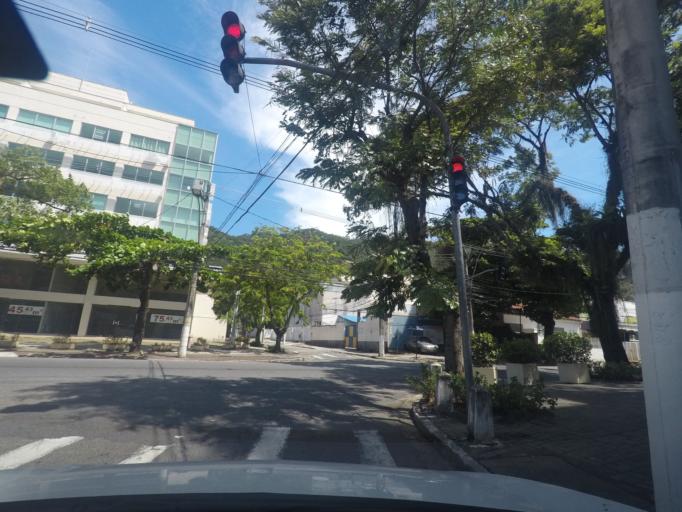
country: BR
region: Rio de Janeiro
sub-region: Niteroi
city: Niteroi
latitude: -22.9176
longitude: -43.0861
